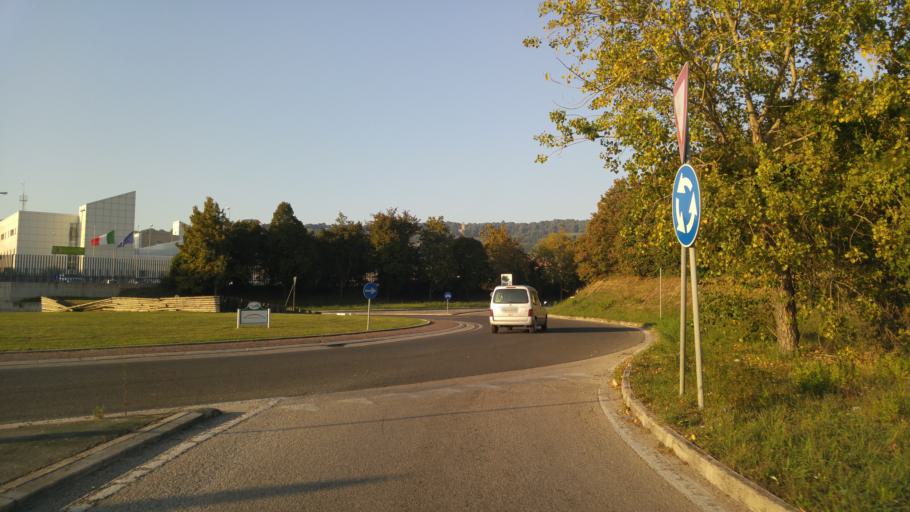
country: IT
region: The Marches
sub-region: Provincia di Pesaro e Urbino
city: Pesaro
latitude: 43.9073
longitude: 12.8737
